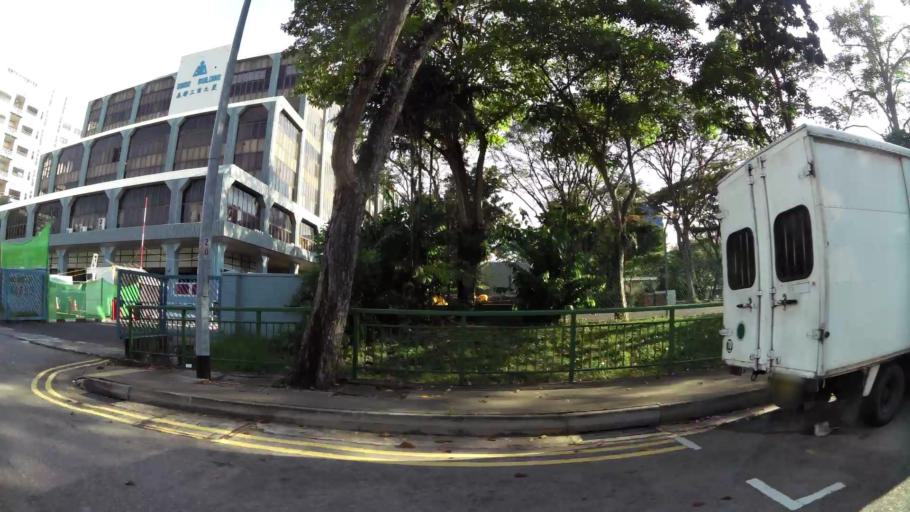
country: SG
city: Singapore
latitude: 1.3257
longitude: 103.8774
